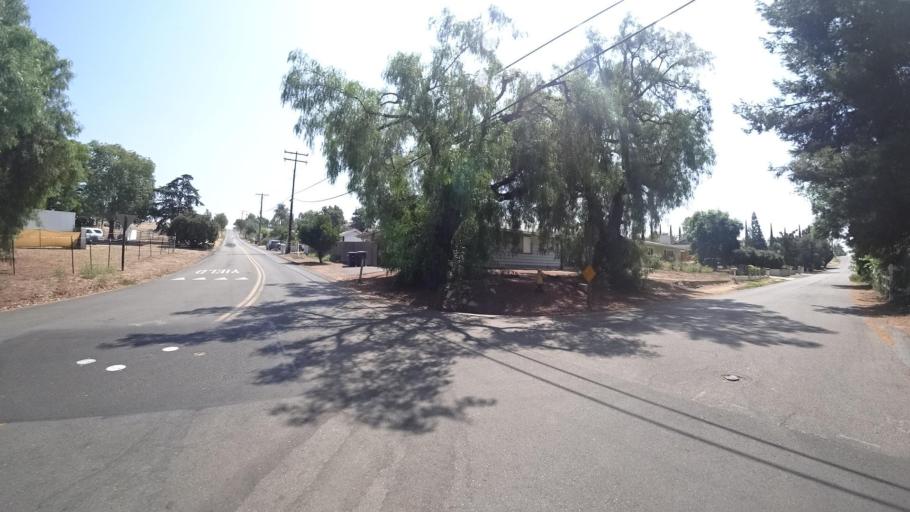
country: US
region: California
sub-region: San Diego County
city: Fallbrook
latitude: 33.3620
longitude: -117.2362
